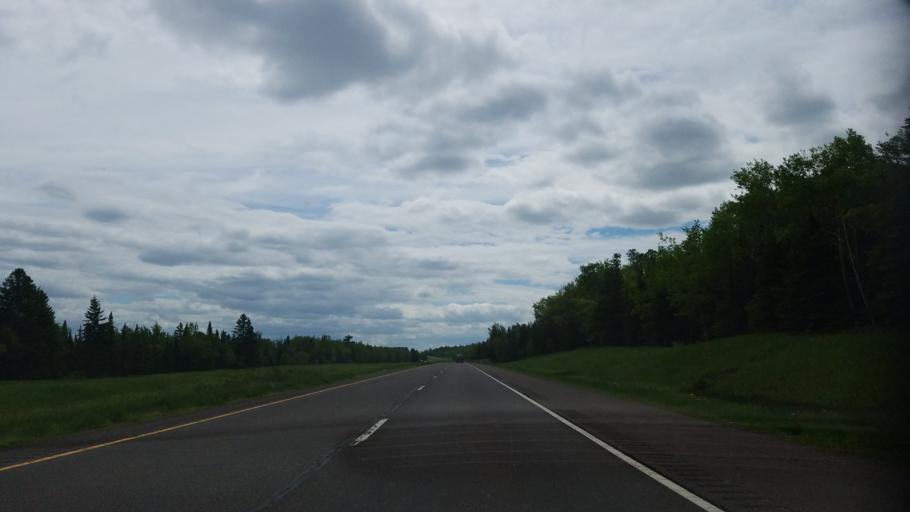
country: US
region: Minnesota
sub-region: Lake County
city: Two Harbors
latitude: 47.0043
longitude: -91.7195
